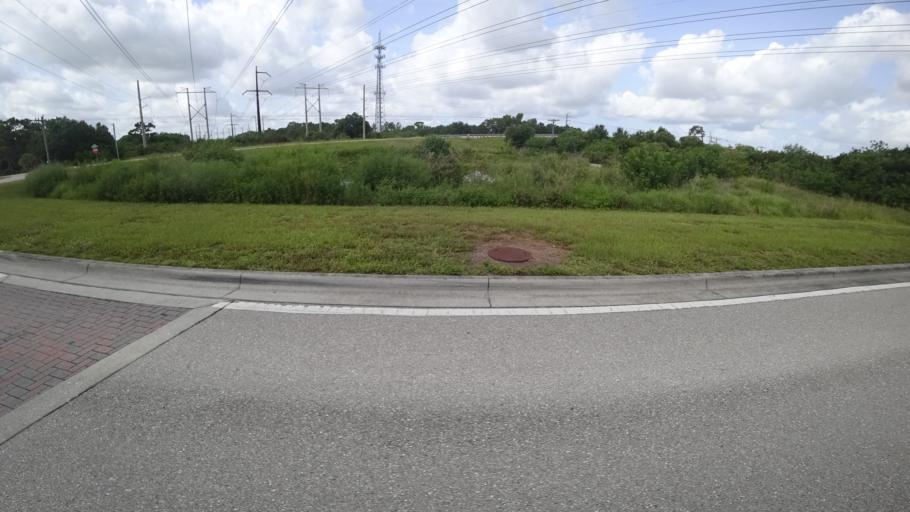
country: US
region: Florida
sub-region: Sarasota County
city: The Meadows
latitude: 27.4186
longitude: -82.4543
